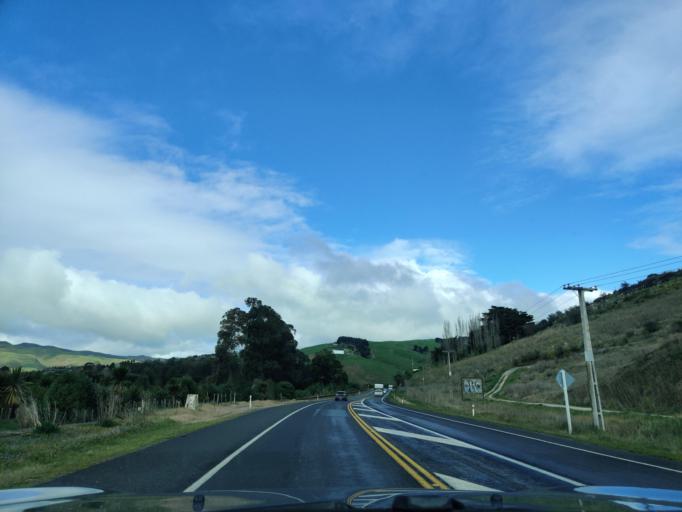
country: NZ
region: Hawke's Bay
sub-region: Hastings District
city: Hastings
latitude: -39.6986
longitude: 176.7935
